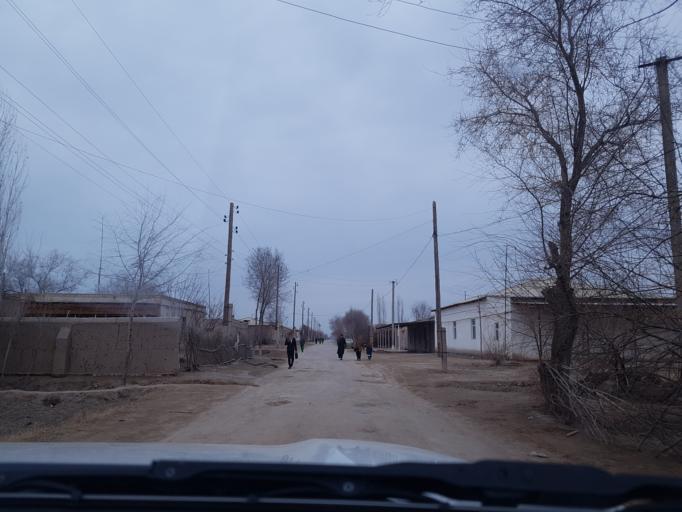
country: TM
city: Akdepe
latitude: 41.9827
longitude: 59.4742
